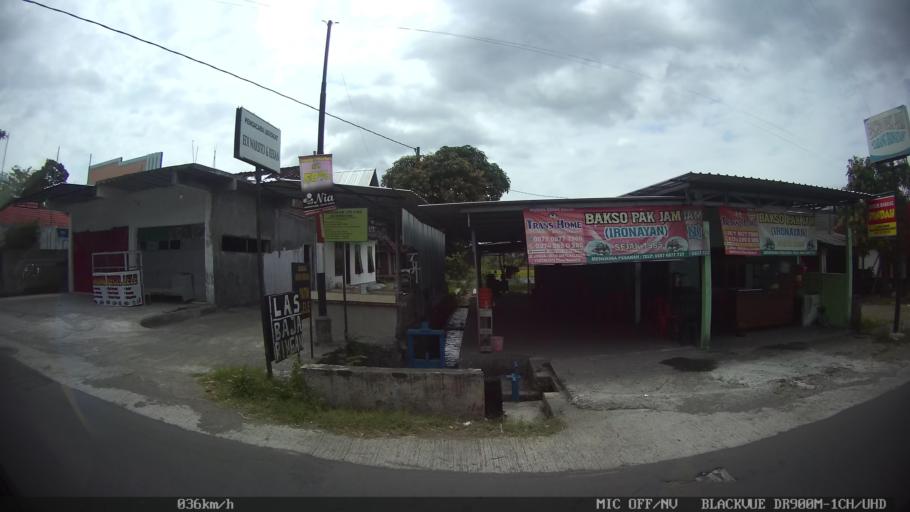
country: ID
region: Daerah Istimewa Yogyakarta
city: Depok
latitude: -7.8072
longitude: 110.4435
